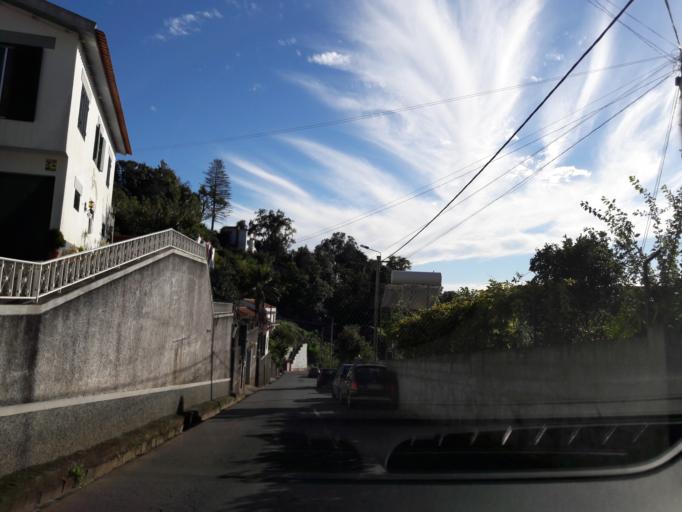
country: PT
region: Madeira
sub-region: Funchal
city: Nossa Senhora do Monte
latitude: 32.6766
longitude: -16.9097
